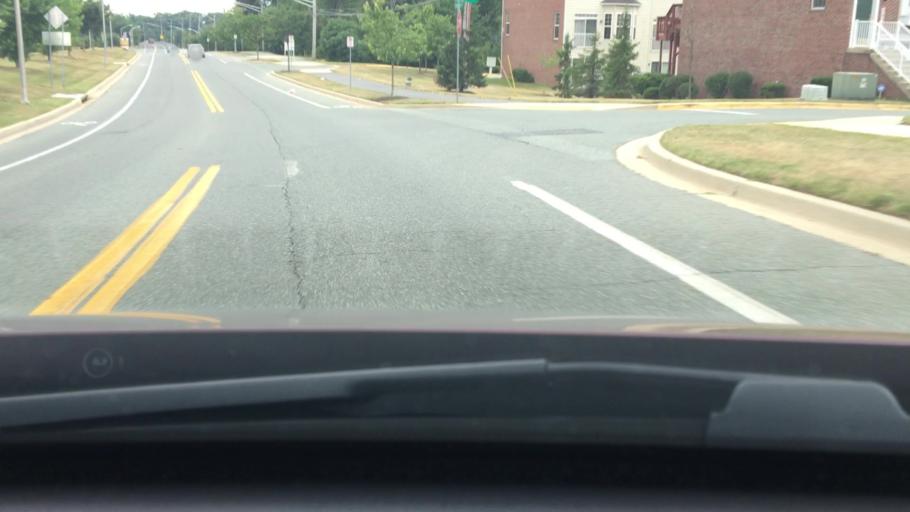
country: US
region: Maryland
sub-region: Prince George's County
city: Calverton
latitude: 39.0819
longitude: -76.9306
